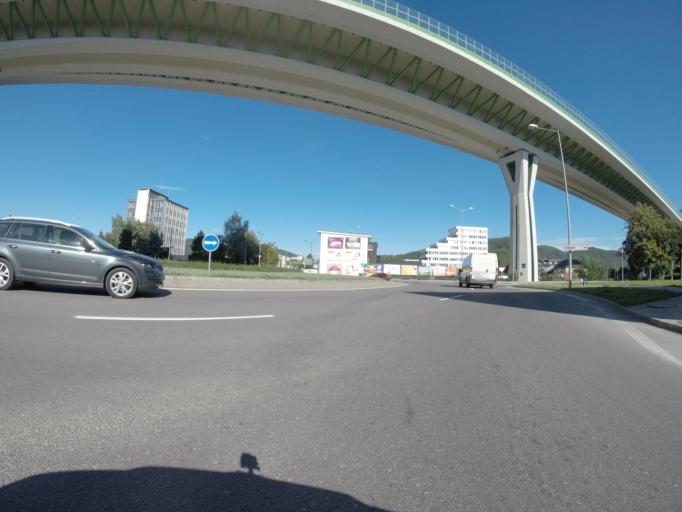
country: SK
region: Trenciansky
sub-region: Okres Povazska Bystrica
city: Povazska Bystrica
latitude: 49.1177
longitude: 18.4391
